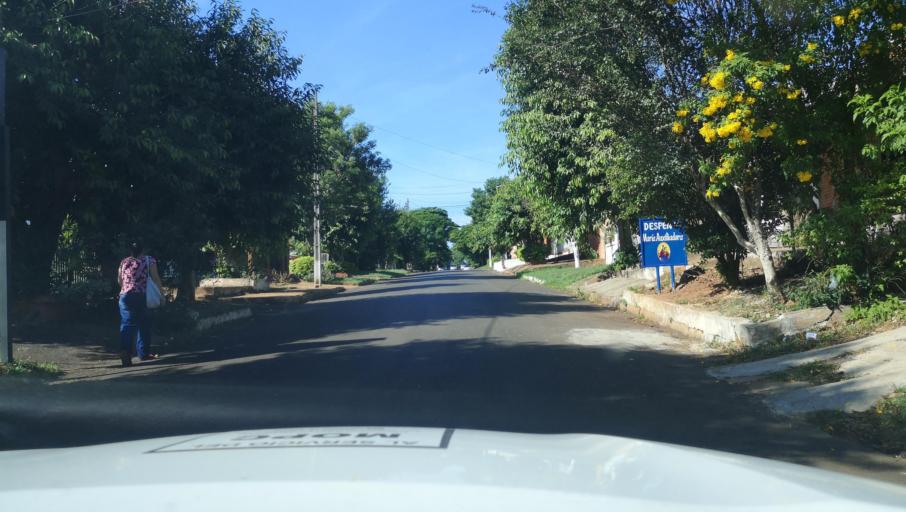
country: PY
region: Misiones
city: Santa Maria
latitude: -26.8861
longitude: -57.0167
